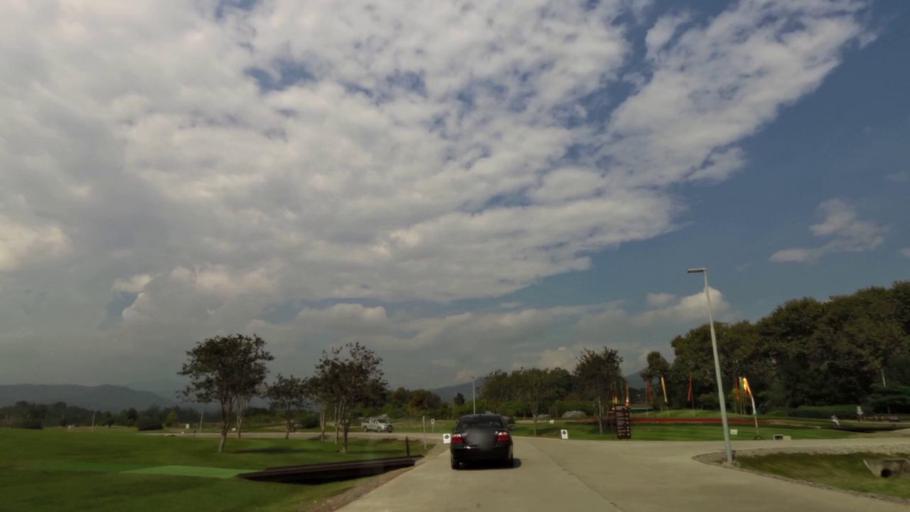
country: TH
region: Chiang Rai
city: Mae Lao
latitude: 19.8532
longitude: 99.7441
